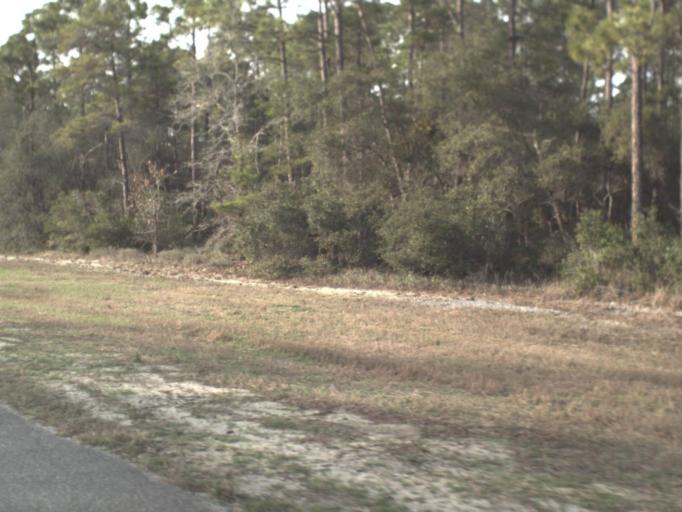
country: US
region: Florida
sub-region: Bay County
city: Mexico Beach
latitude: 29.9657
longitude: -85.4483
